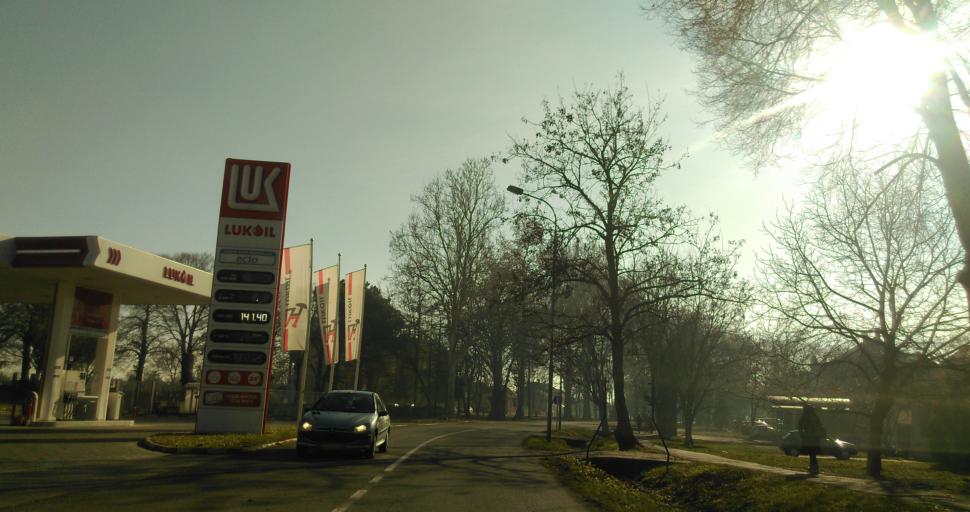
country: RS
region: Autonomna Pokrajina Vojvodina
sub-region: Sremski Okrug
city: Ruma
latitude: 45.0013
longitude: 19.8229
